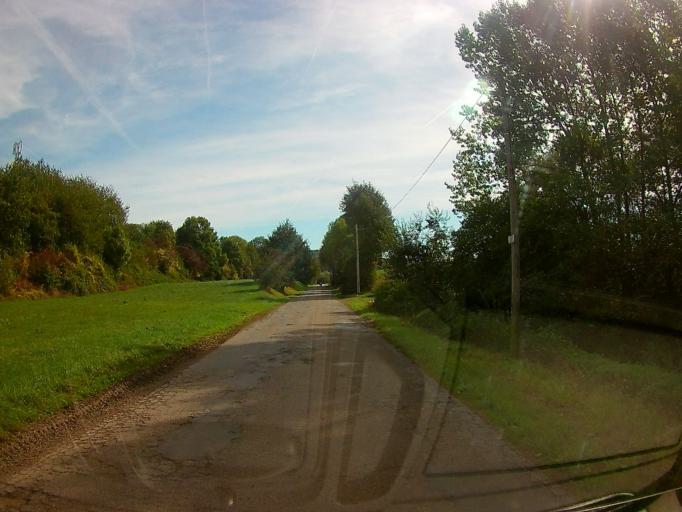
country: BE
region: Wallonia
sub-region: Province de Liege
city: Aubel
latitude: 50.7399
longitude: 5.8880
